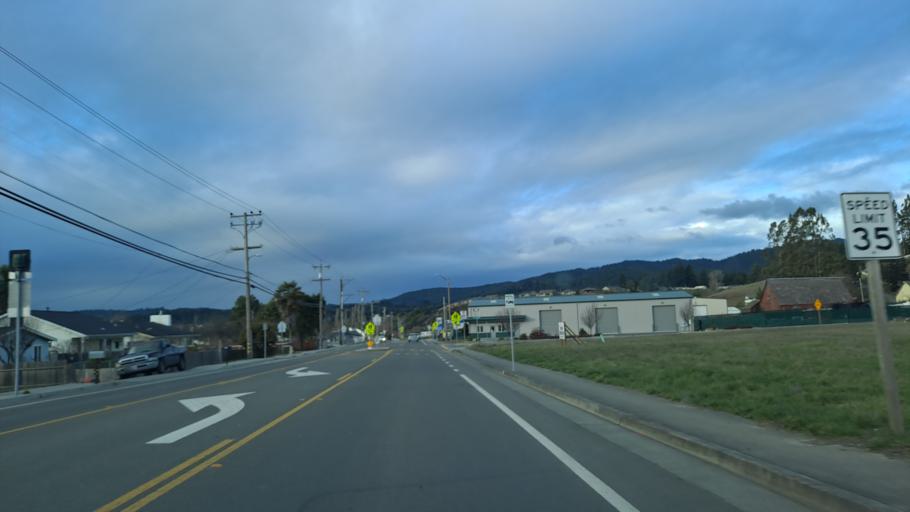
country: US
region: California
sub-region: Humboldt County
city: Fortuna
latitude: 40.5809
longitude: -124.1304
